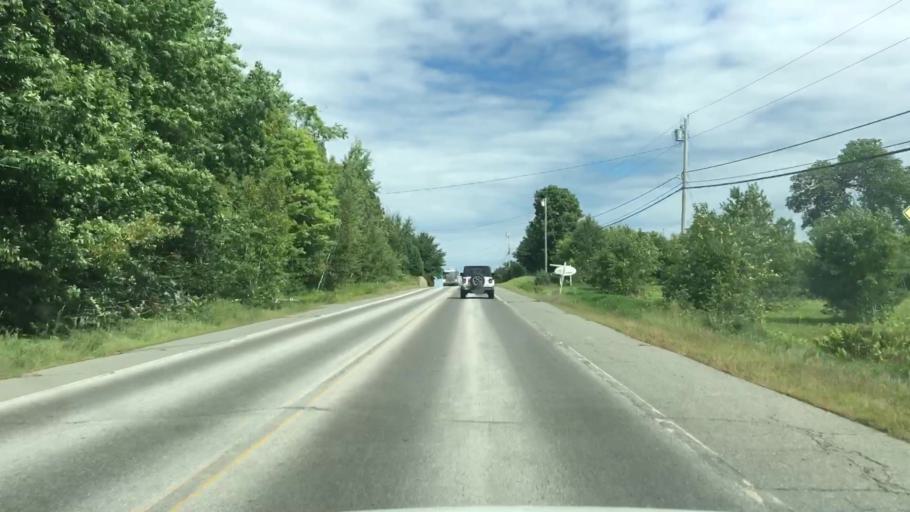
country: US
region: Maine
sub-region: Piscataquis County
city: Dover-Foxcroft
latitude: 45.1618
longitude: -69.2317
